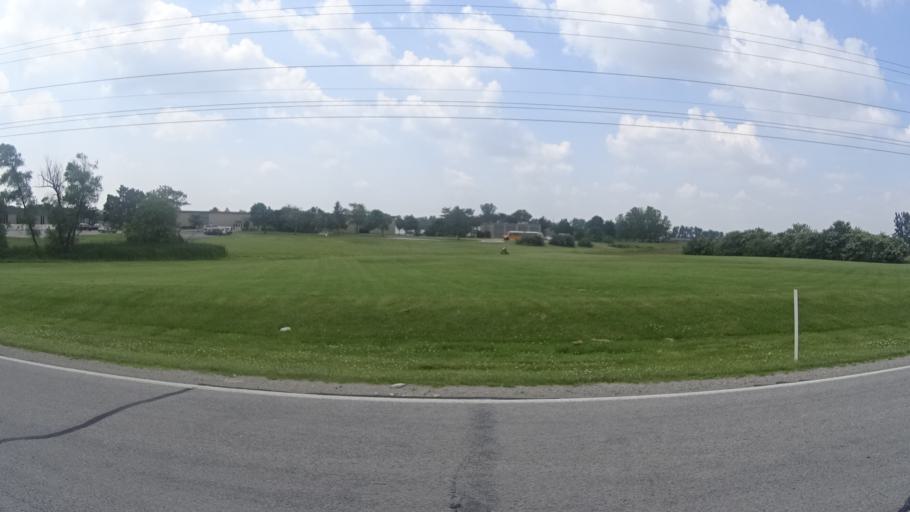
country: US
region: Ohio
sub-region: Erie County
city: Milan
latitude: 41.3336
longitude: -82.6328
